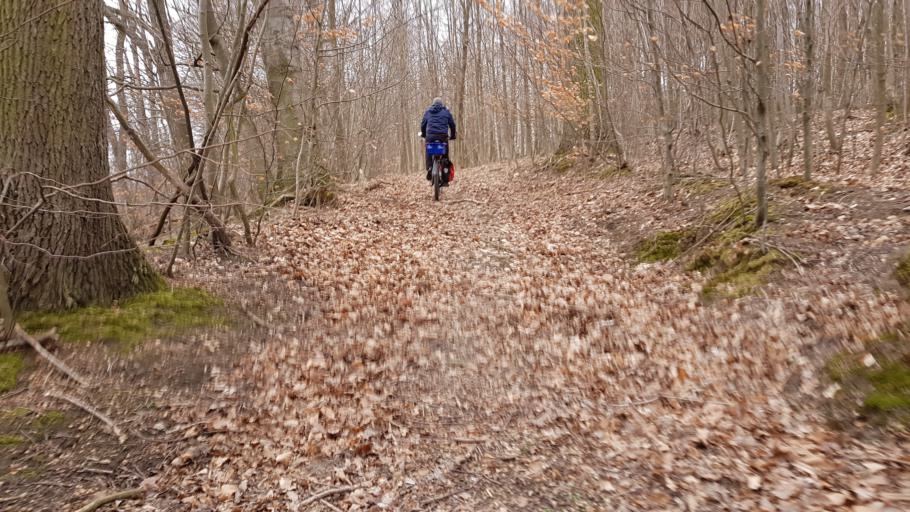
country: PL
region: West Pomeranian Voivodeship
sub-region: Powiat pyrzycki
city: Kozielice
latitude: 53.0740
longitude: 14.7506
